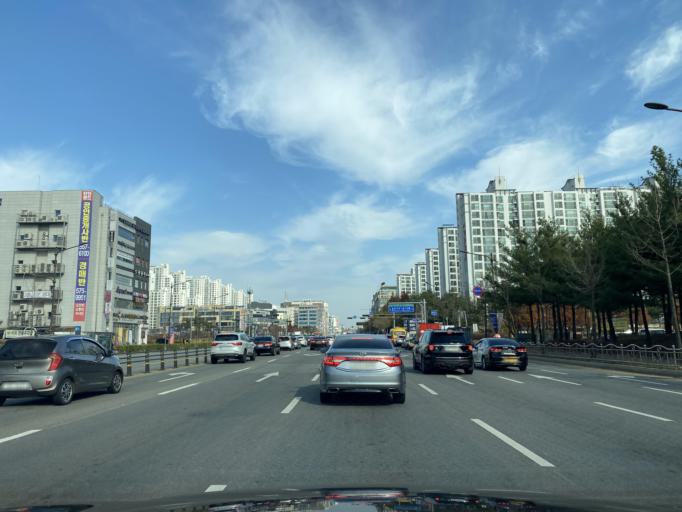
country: KR
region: Chungcheongnam-do
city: Cheonan
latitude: 36.8064
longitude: 127.1069
